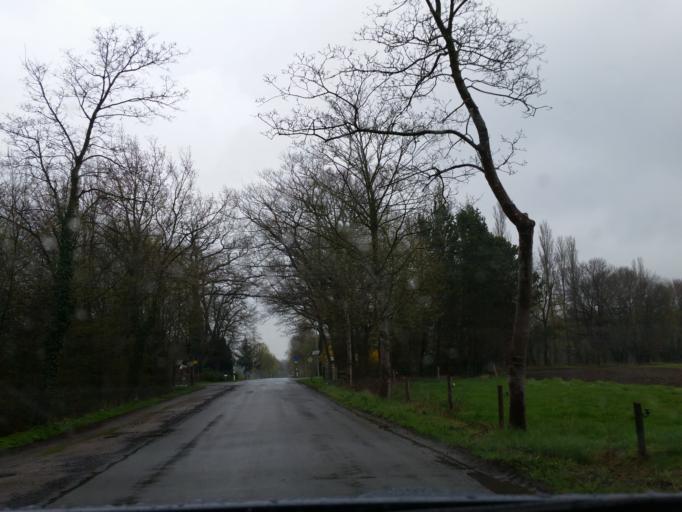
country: DE
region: Lower Saxony
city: Hipstedt
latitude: 53.4828
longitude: 8.9690
